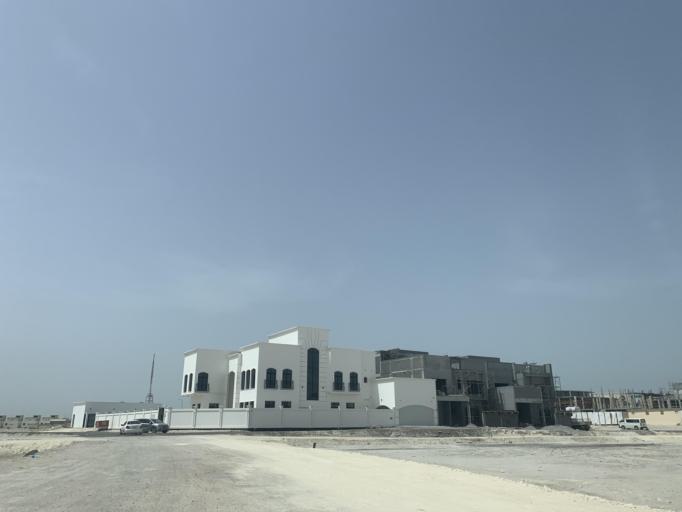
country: BH
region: Northern
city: Madinat `Isa
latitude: 26.1539
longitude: 50.5614
